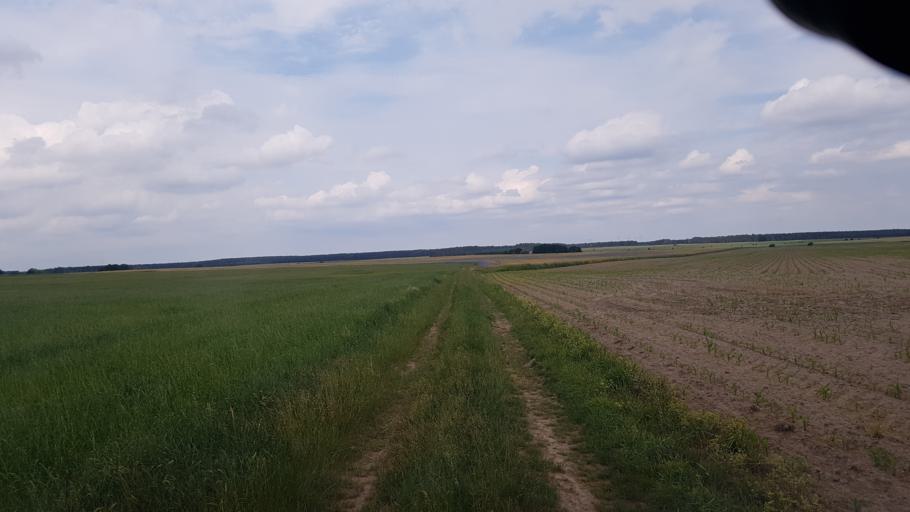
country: DE
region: Brandenburg
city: Dahme
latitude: 51.8826
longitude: 13.3974
